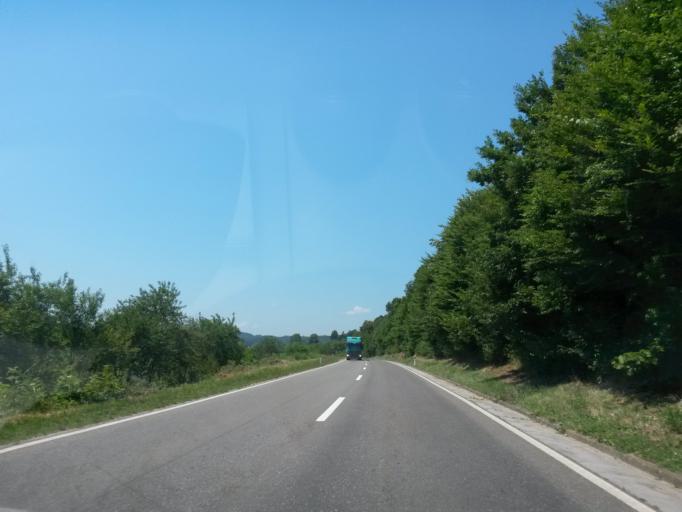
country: BA
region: Federation of Bosnia and Herzegovina
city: Odzak
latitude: 44.9687
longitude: 18.2463
